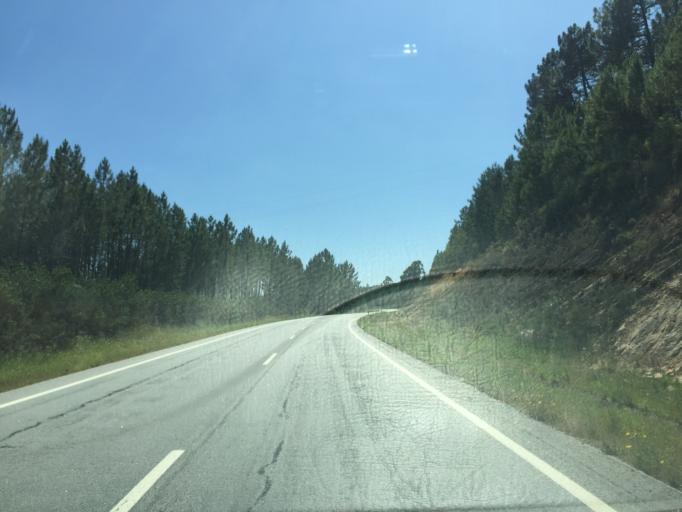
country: PT
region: Castelo Branco
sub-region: Vila de Rei
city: Vila de Rei
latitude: 39.5821
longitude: -8.1456
